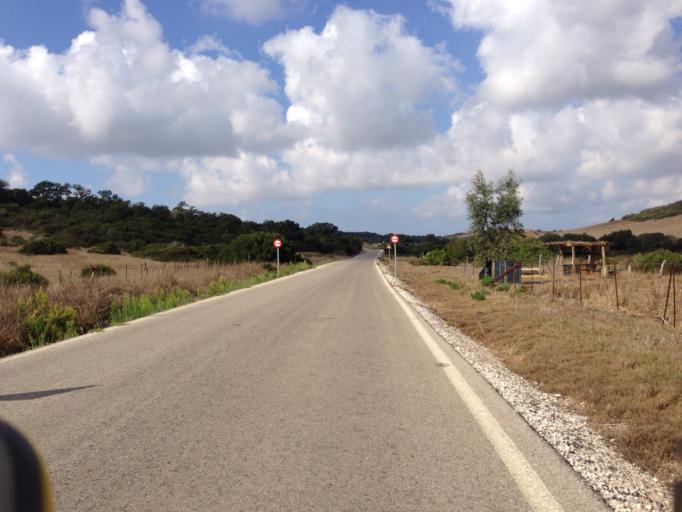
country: ES
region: Andalusia
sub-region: Provincia de Cadiz
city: Conil de la Frontera
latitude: 36.3438
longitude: -6.0111
